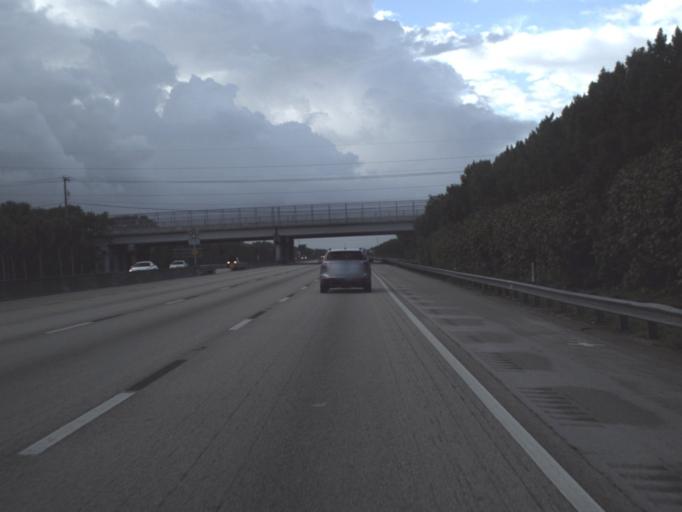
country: US
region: Florida
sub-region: Palm Beach County
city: Boca Pointe
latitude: 26.3519
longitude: -80.1707
